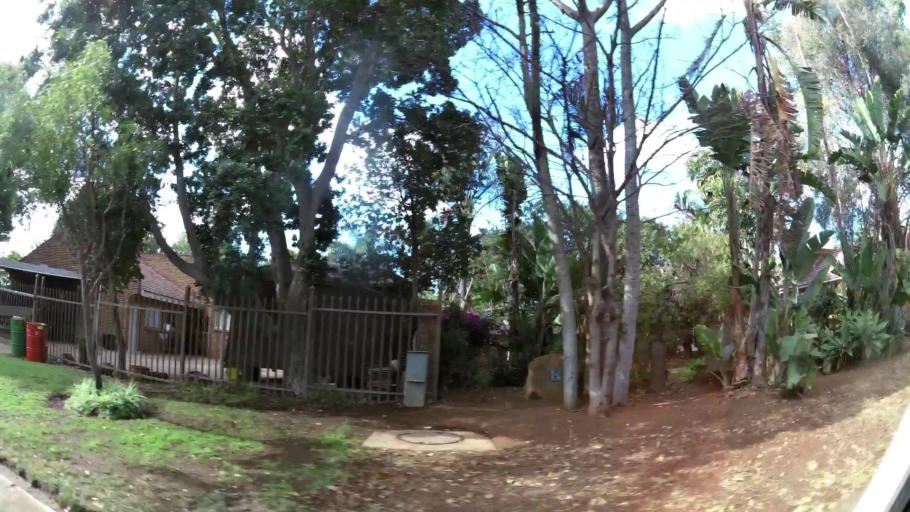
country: ZA
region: Limpopo
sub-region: Capricorn District Municipality
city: Polokwane
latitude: -23.8974
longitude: 29.4797
